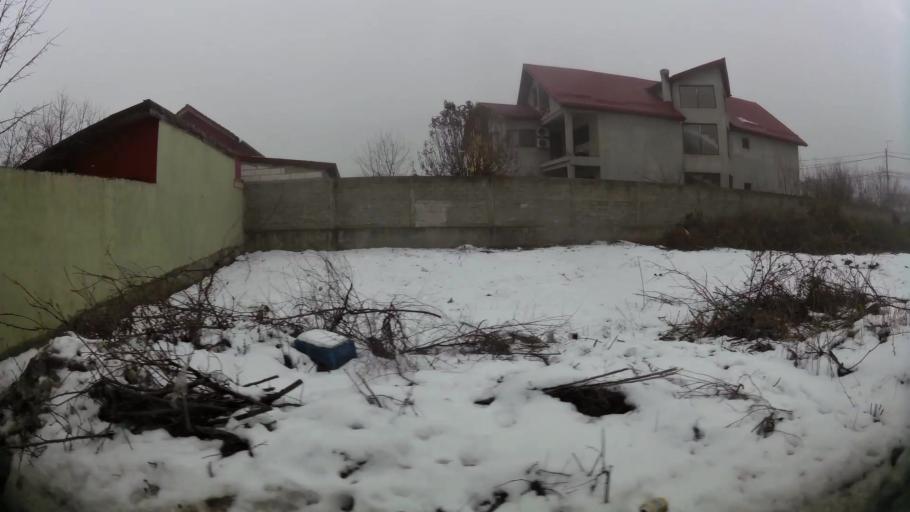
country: RO
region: Ilfov
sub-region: Comuna Chiajna
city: Rosu
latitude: 44.4531
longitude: 25.9931
